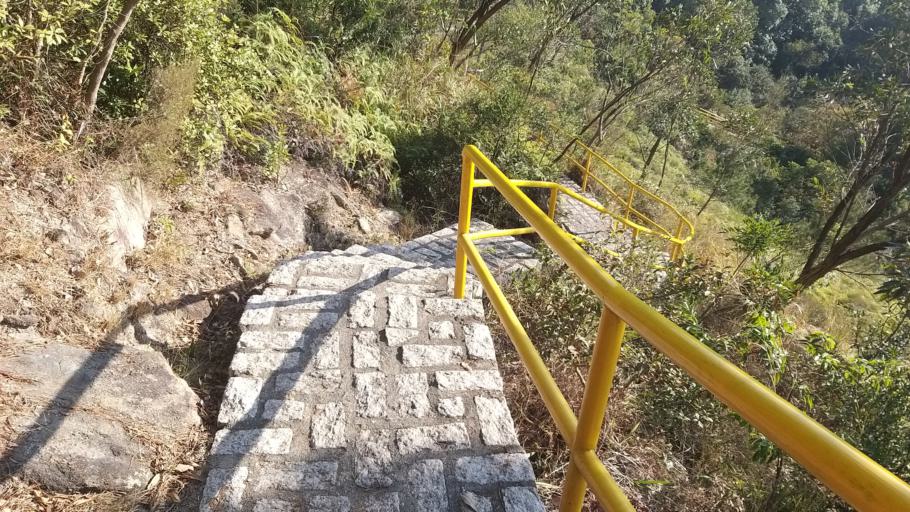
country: HK
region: Tuen Mun
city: Tuen Mun
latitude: 22.3956
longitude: 113.9830
